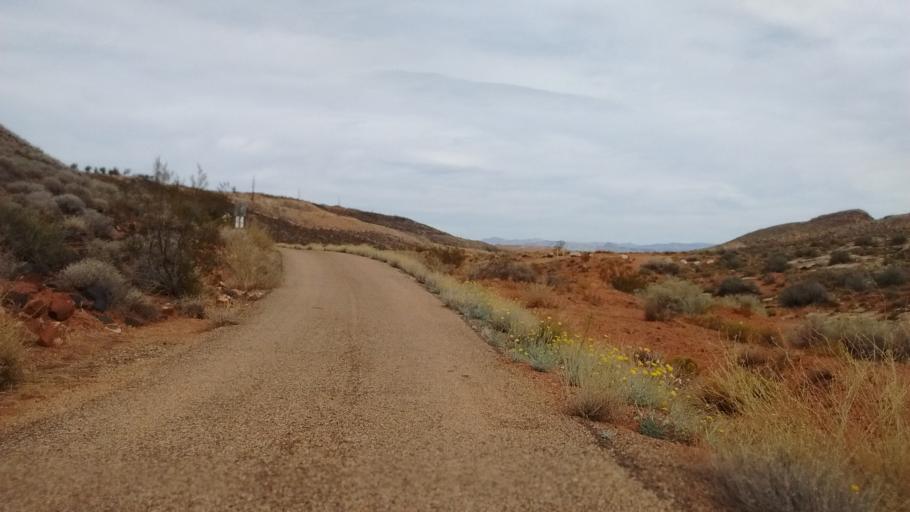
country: US
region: Utah
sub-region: Washington County
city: Washington
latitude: 37.1324
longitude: -113.4700
